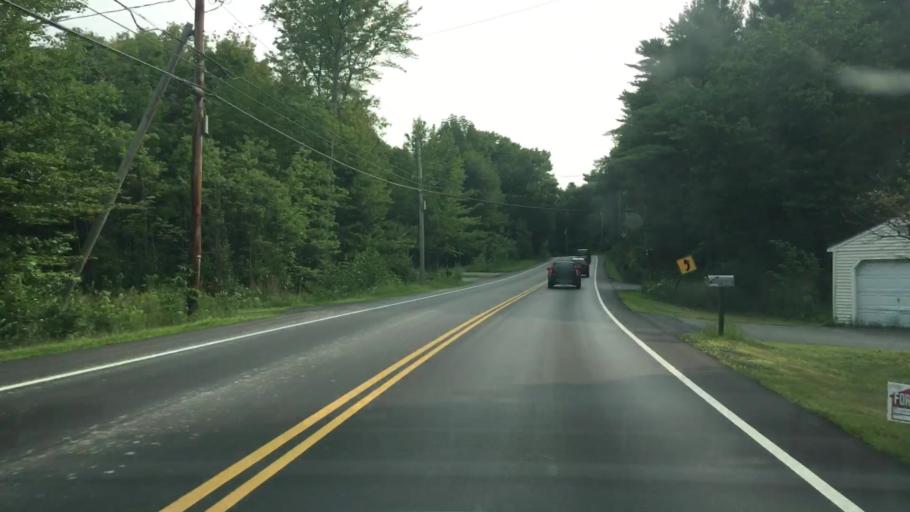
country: US
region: Maine
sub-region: Kennebec County
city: Chelsea
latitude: 44.2440
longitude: -69.7279
